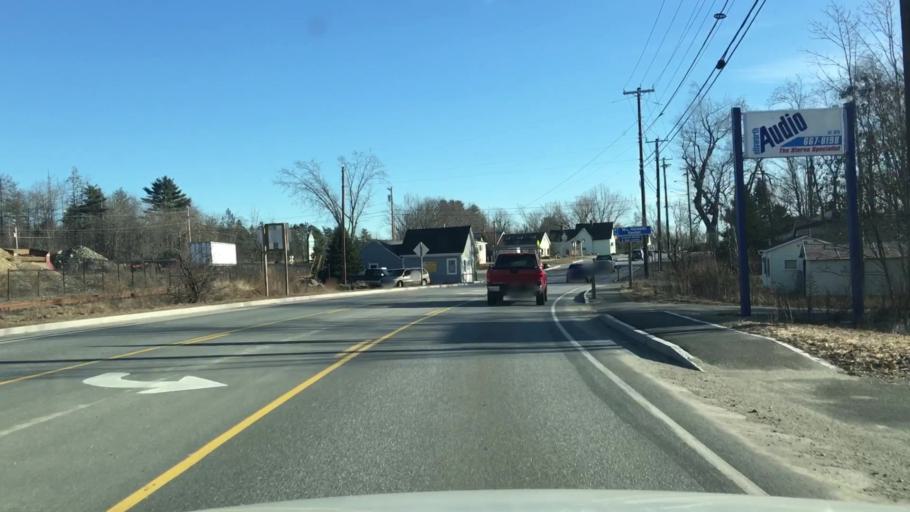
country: US
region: Maine
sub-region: Hancock County
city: Ellsworth
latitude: 44.5621
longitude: -68.4386
